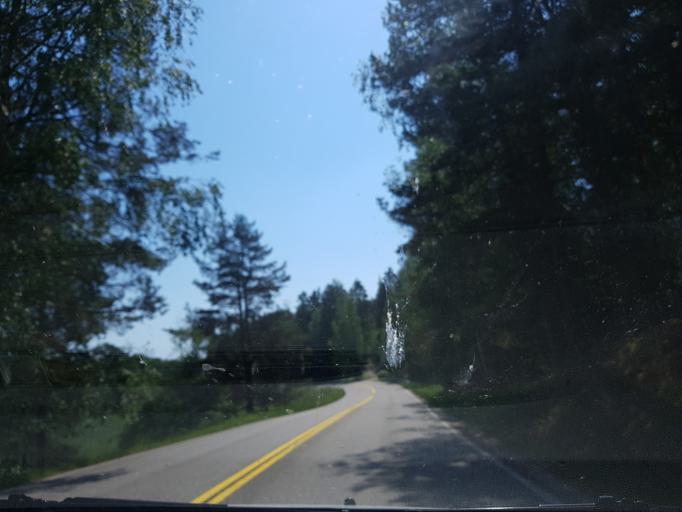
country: FI
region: Uusimaa
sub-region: Helsinki
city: Vihti
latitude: 60.3175
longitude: 24.4036
